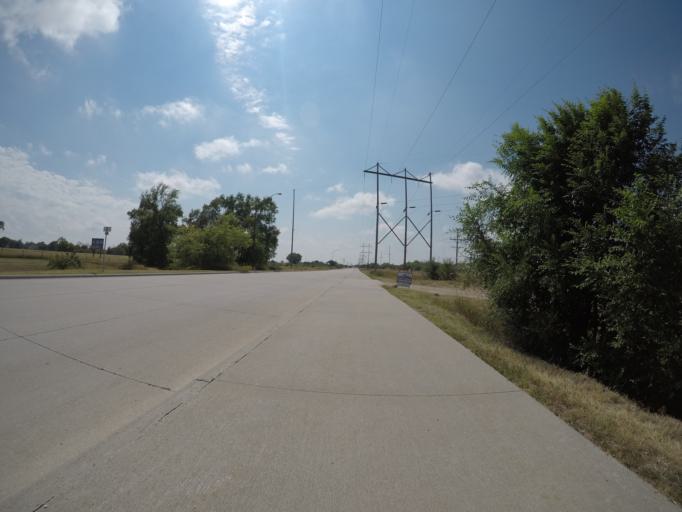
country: US
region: Nebraska
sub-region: Buffalo County
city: Kearney
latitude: 40.6706
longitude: -99.0722
